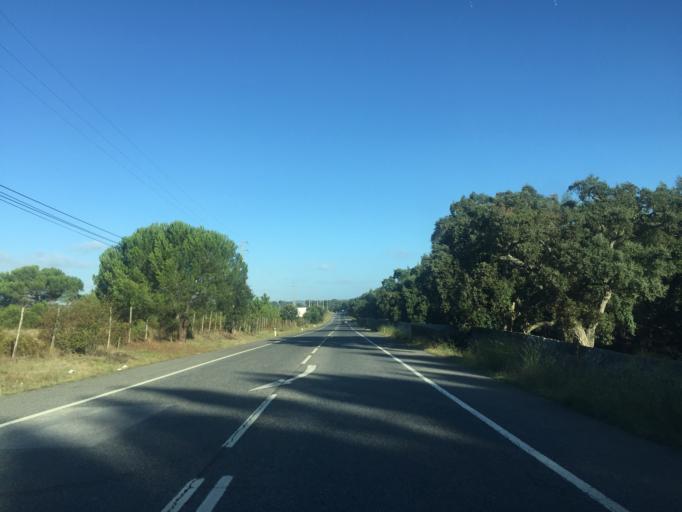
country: PT
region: Lisbon
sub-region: Azambuja
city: Alcoentre
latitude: 39.1764
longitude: -8.9370
